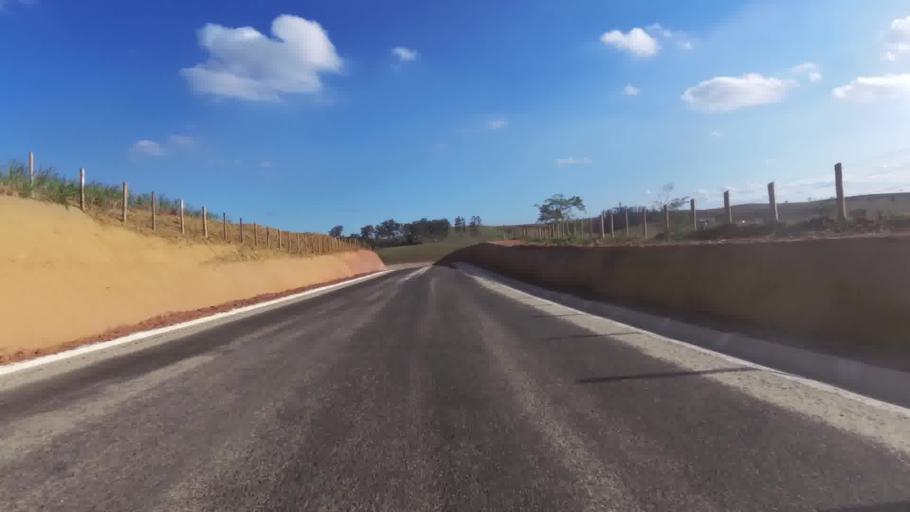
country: BR
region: Espirito Santo
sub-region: Marataizes
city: Marataizes
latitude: -21.1330
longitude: -41.0547
